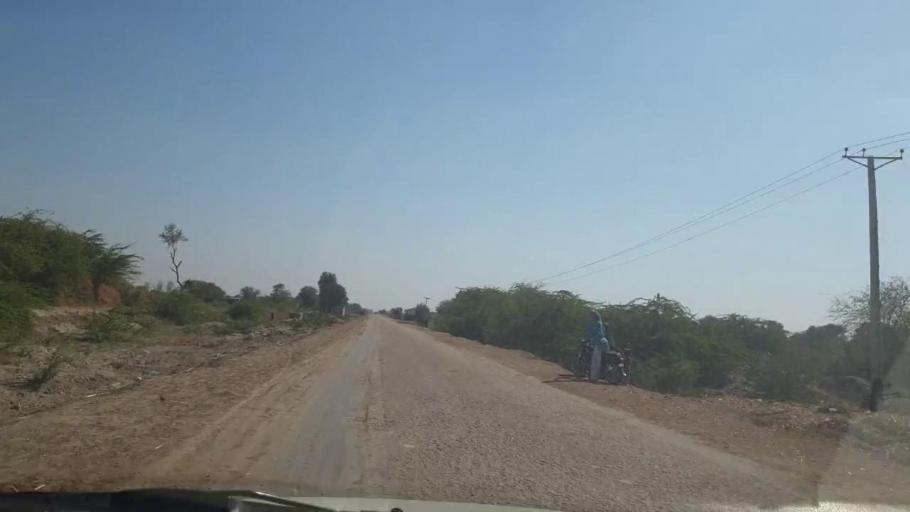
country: PK
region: Sindh
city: Mirpur Khas
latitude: 25.4729
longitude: 69.1755
